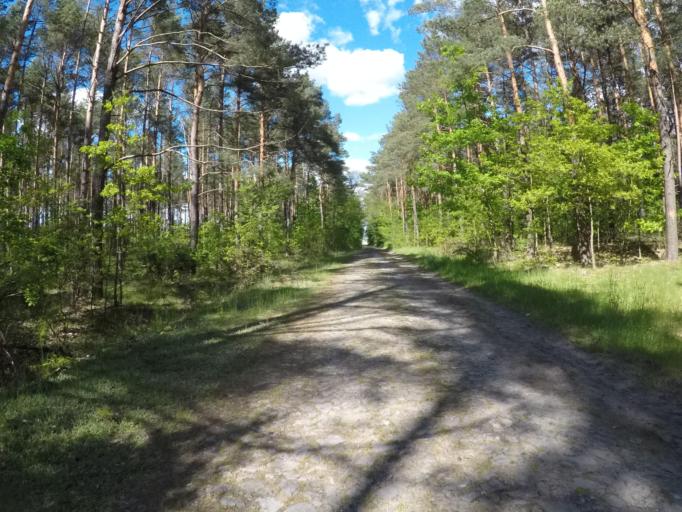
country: PL
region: Swietokrzyskie
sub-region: Powiat kielecki
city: Kostomloty Drugie
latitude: 50.8947
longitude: 20.5458
